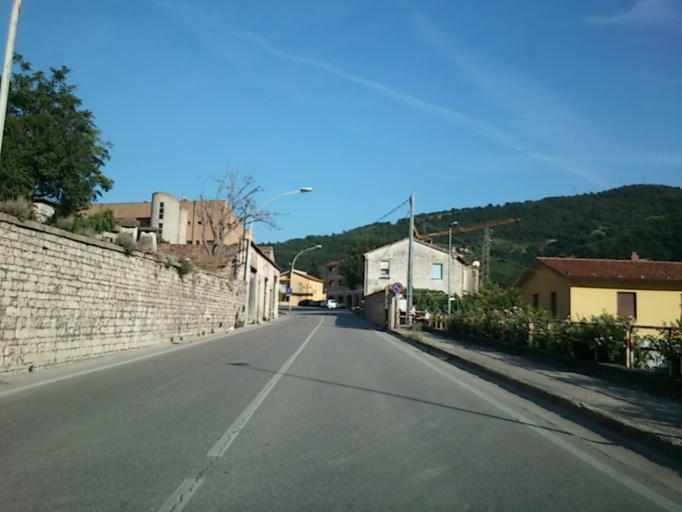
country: IT
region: The Marches
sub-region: Provincia di Pesaro e Urbino
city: Fossombrone
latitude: 43.6880
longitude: 12.8057
